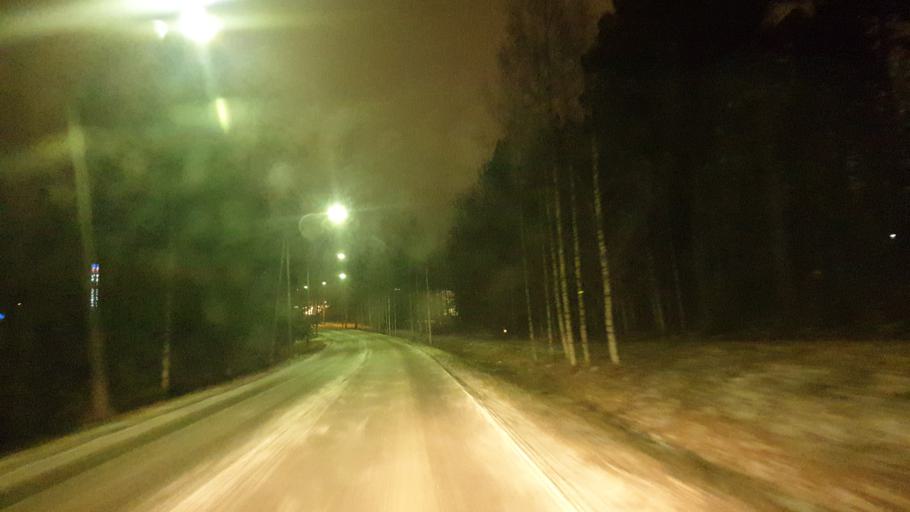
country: FI
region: Southern Savonia
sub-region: Savonlinna
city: Savonlinna
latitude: 61.8631
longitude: 28.9446
